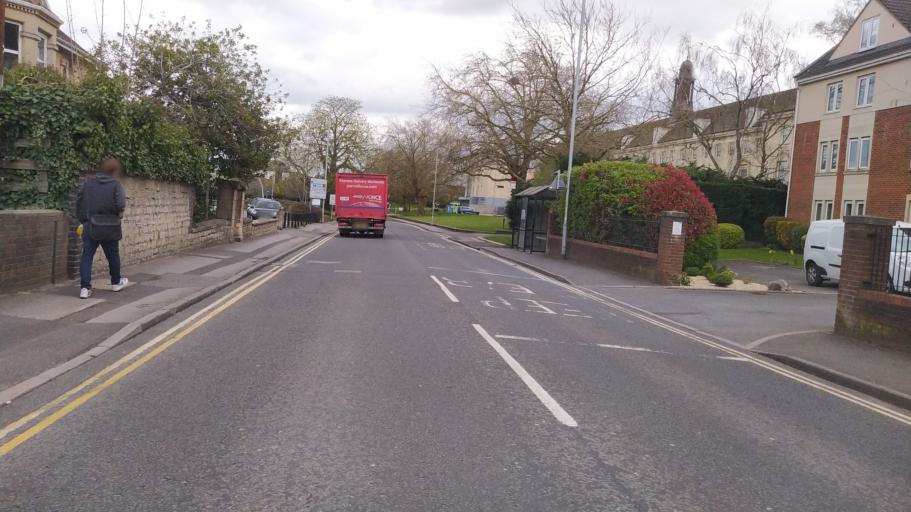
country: GB
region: England
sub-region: Wiltshire
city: Trowbridge
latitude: 51.3182
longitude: -2.2108
